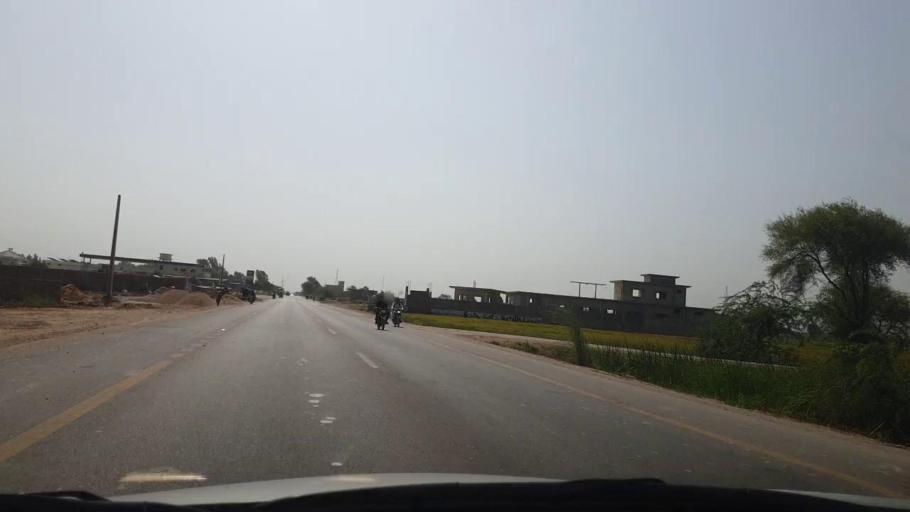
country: PK
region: Sindh
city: Tando Muhammad Khan
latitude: 25.1047
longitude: 68.5862
